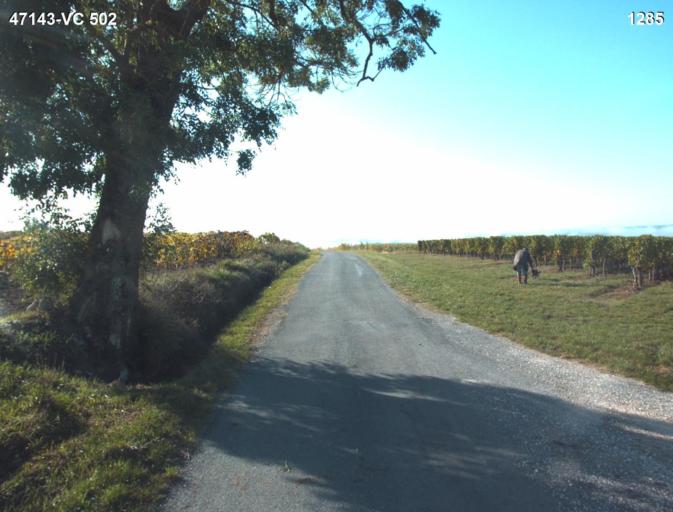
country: FR
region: Aquitaine
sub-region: Departement du Lot-et-Garonne
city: Vianne
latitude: 44.1750
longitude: 0.3266
